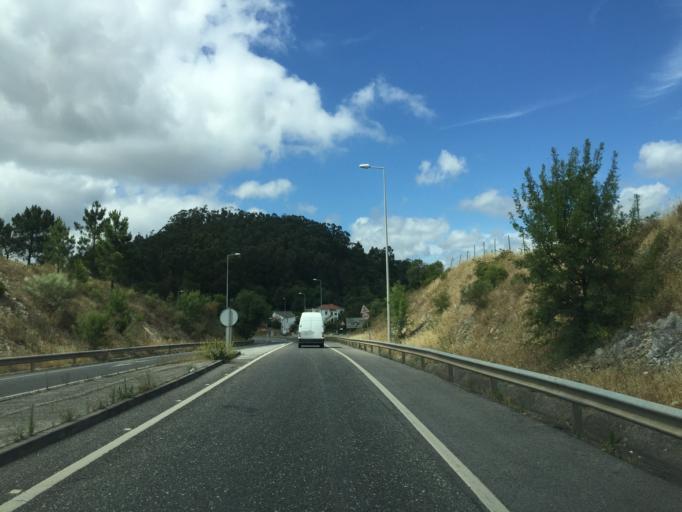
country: PT
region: Lisbon
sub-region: Odivelas
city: Famoes
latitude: 38.7865
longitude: -9.2341
